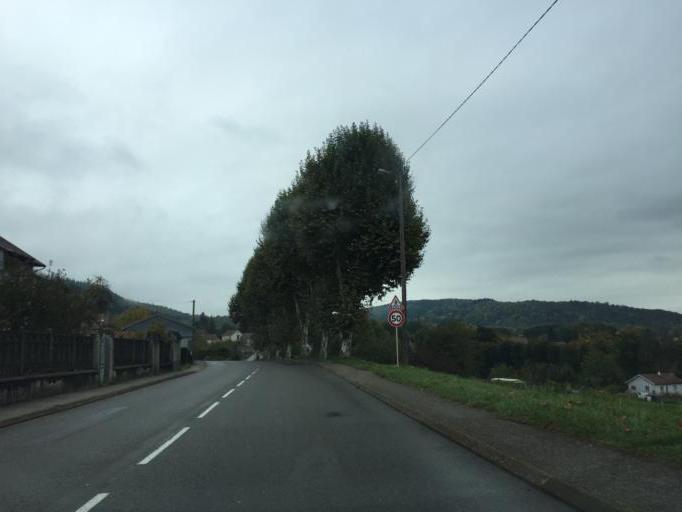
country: FR
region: Franche-Comte
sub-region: Departement du Jura
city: Orgelet
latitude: 46.5223
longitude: 5.6154
